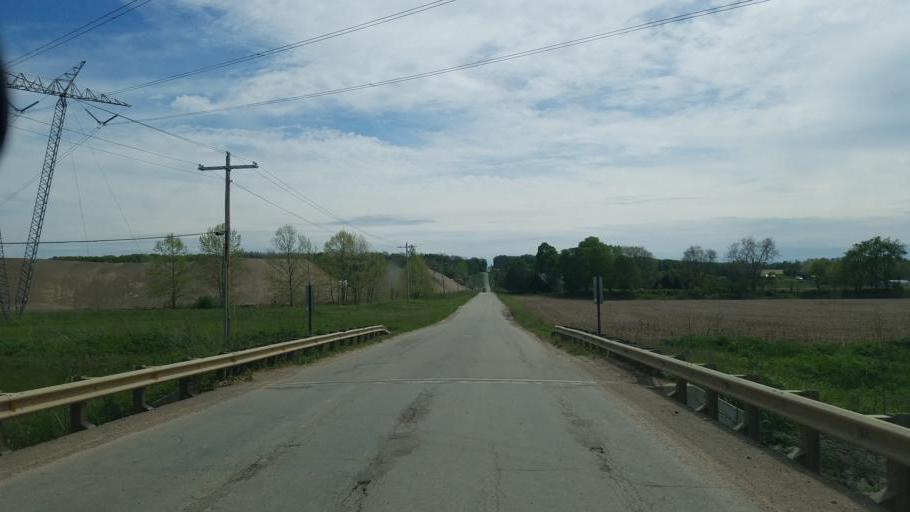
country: US
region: Ohio
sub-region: Knox County
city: Gambier
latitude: 40.3843
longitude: -82.3530
